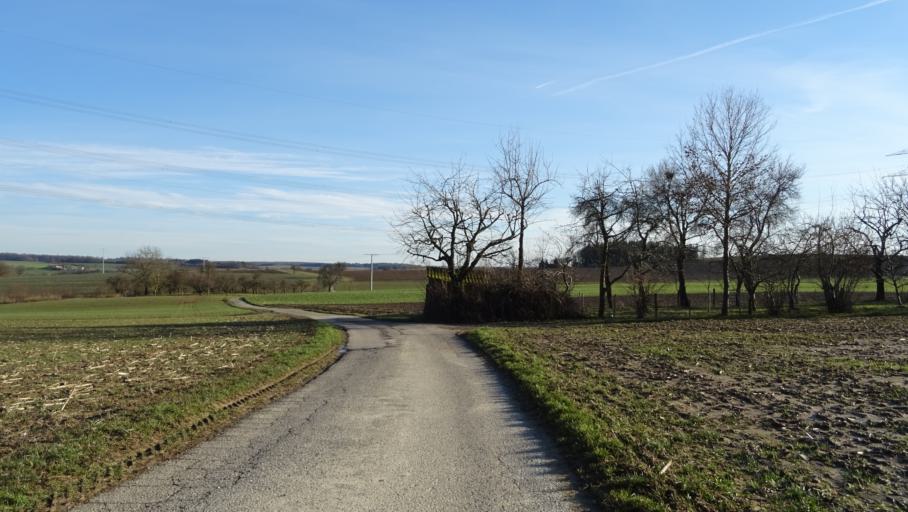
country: DE
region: Baden-Wuerttemberg
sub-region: Karlsruhe Region
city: Billigheim
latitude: 49.4162
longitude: 9.2651
